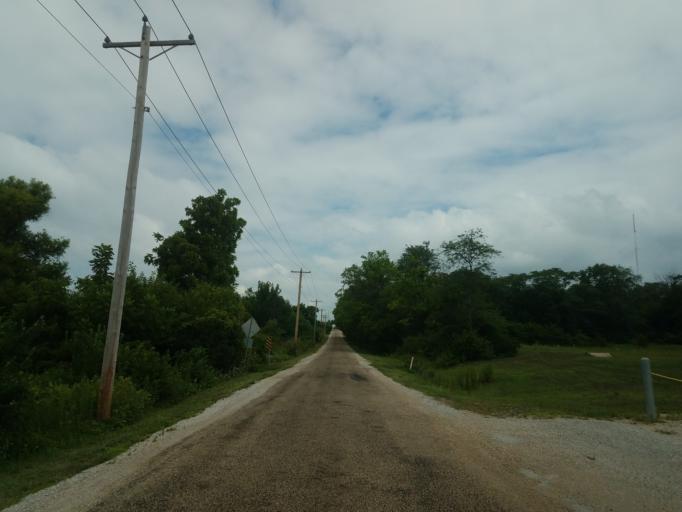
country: US
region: Illinois
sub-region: McLean County
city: Bloomington
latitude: 40.4455
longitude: -89.0152
